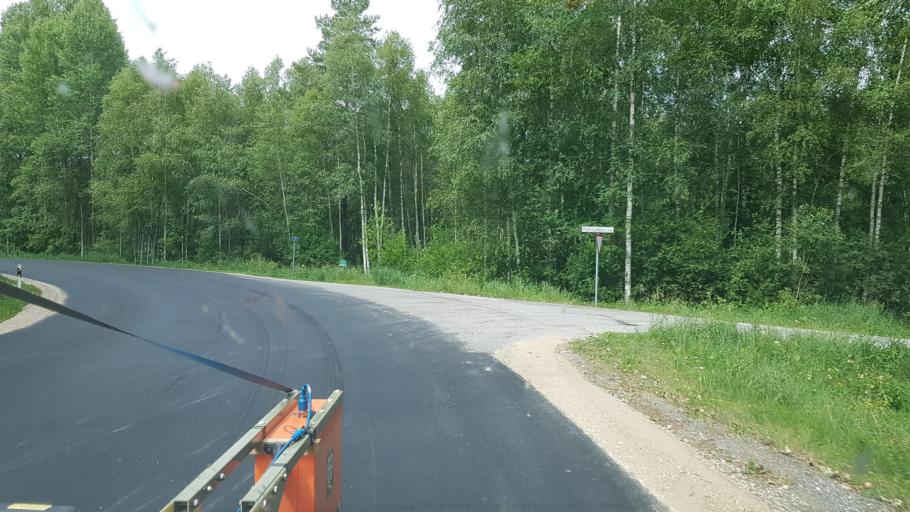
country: EE
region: Paernumaa
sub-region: Audru vald
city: Audru
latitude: 58.6235
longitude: 24.2482
